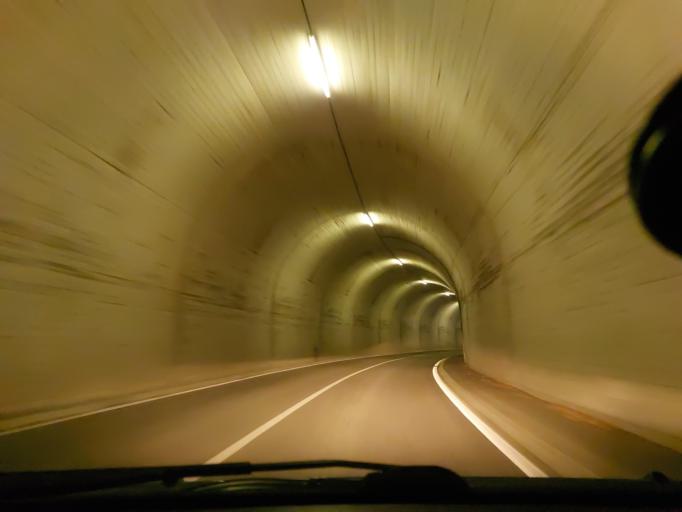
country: CH
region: Valais
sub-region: Martigny District
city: Riddes
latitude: 46.1713
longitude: 7.2495
